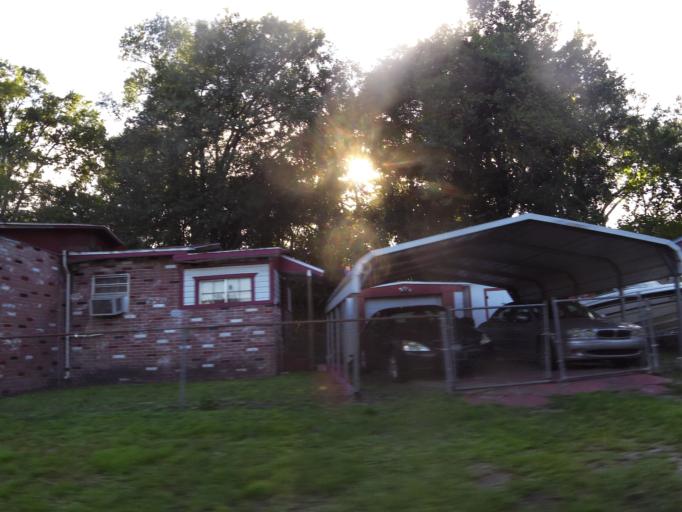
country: US
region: Florida
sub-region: Duval County
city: Jacksonville
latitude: 30.3413
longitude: -81.6910
